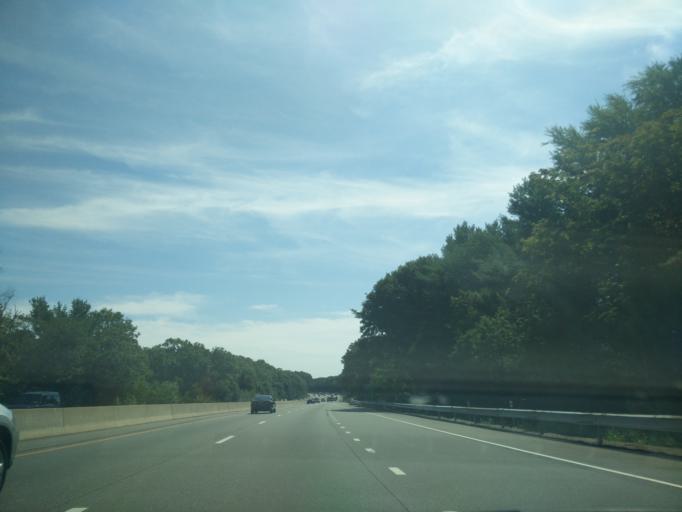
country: US
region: Connecticut
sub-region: New Haven County
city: Madison
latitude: 41.2902
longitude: -72.5663
